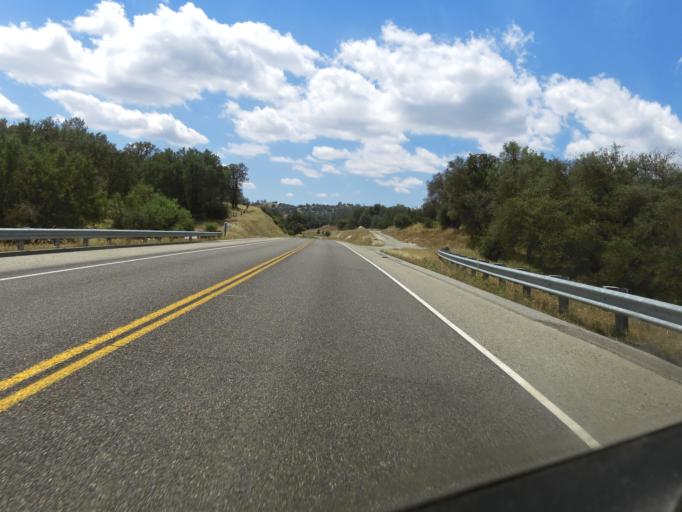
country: US
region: California
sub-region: Madera County
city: Coarsegold
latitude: 37.1522
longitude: -119.6601
